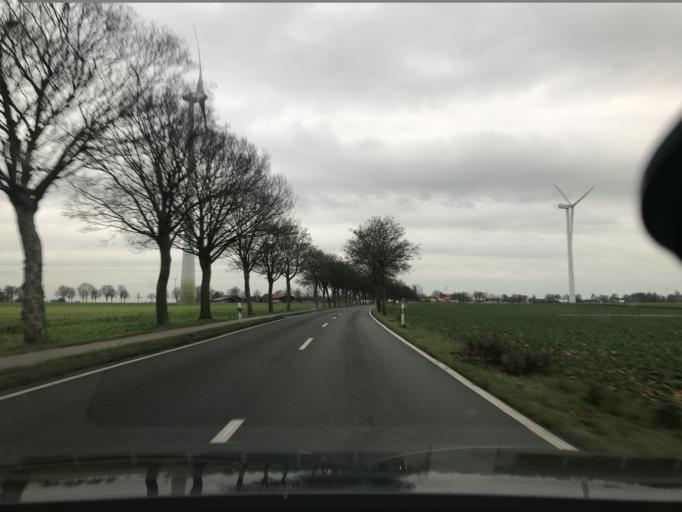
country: DE
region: North Rhine-Westphalia
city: Kalkar
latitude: 51.7113
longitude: 6.2298
